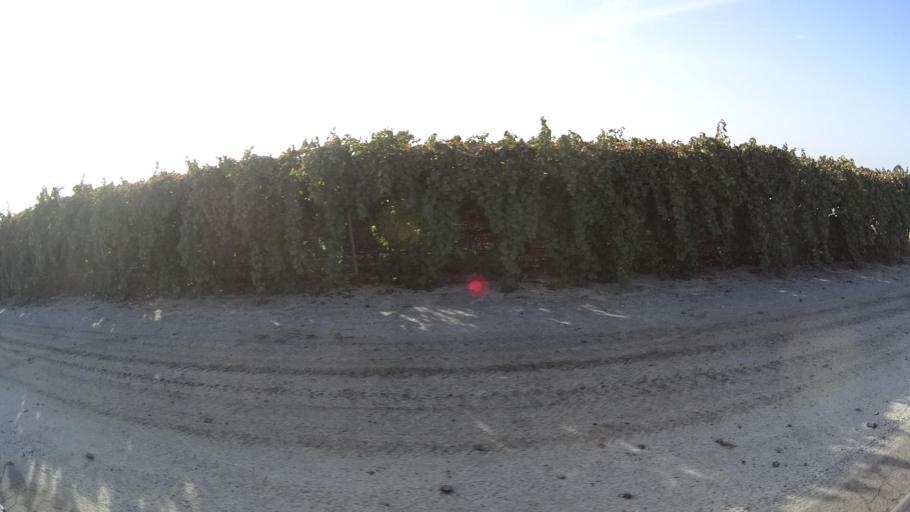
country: US
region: California
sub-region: Kern County
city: McFarland
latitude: 35.6818
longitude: -119.2070
